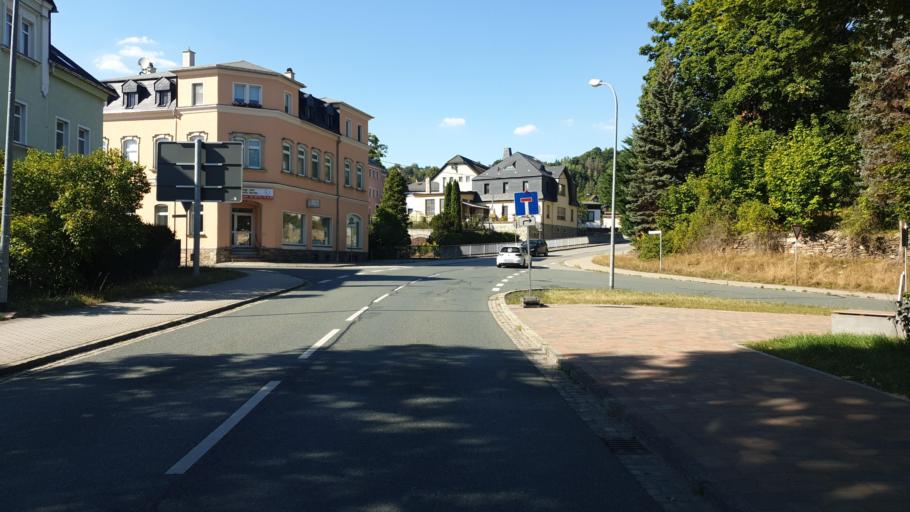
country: DE
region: Saxony
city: Schwarzenberg
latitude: 50.5483
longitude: 12.7811
